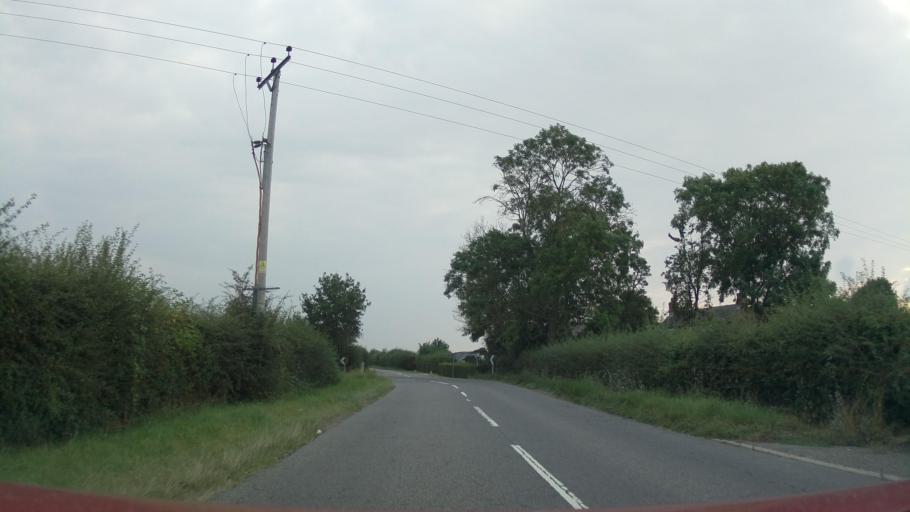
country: GB
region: England
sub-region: Lincolnshire
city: Skellingthorpe
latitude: 53.1349
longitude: -0.6462
